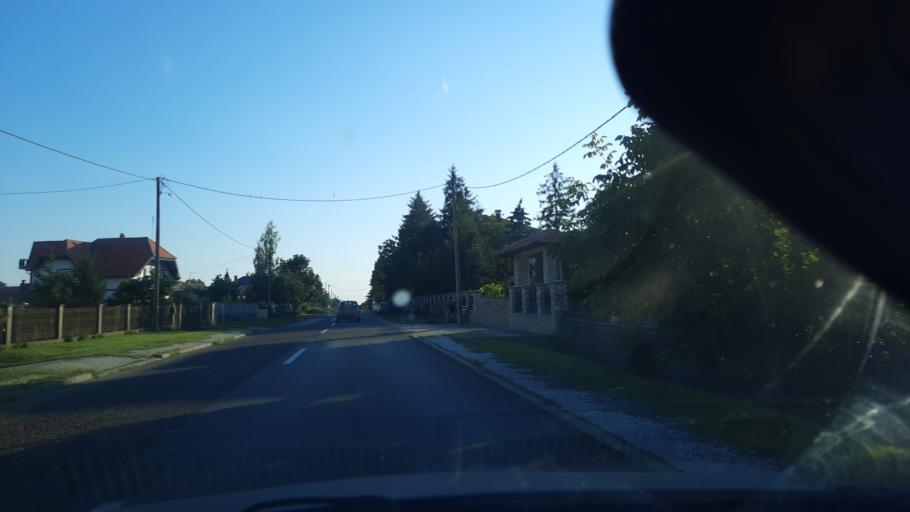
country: RS
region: Central Serbia
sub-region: Branicevski Okrug
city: Malo Crnice
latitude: 44.5836
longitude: 21.3974
